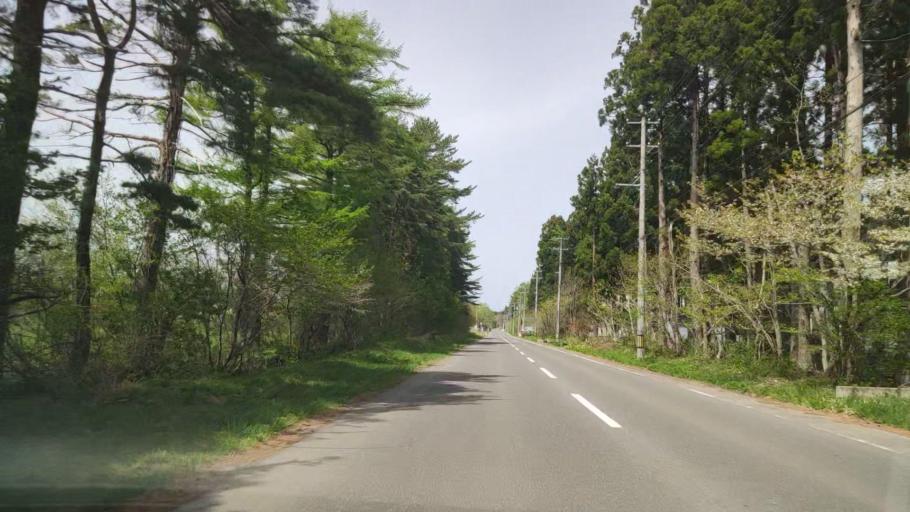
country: JP
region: Aomori
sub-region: Misawa Shi
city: Inuotose
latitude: 40.7158
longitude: 141.1437
